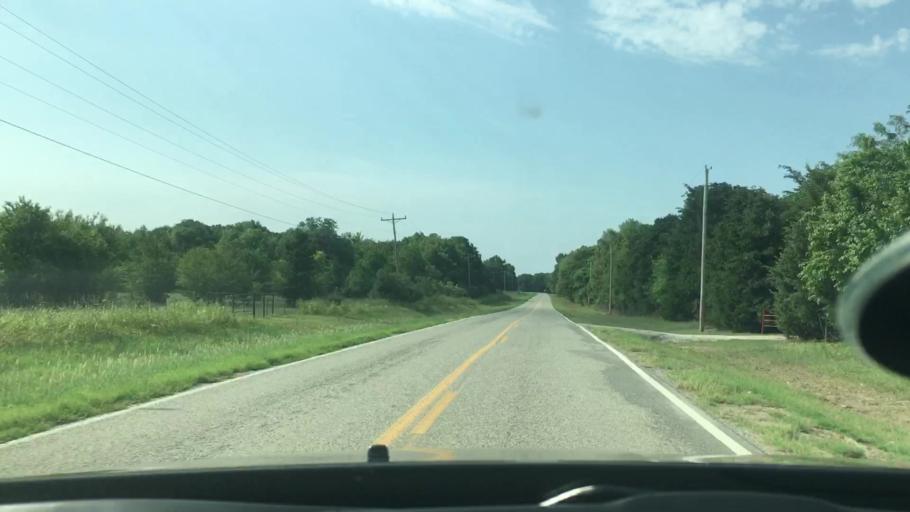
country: US
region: Oklahoma
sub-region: Johnston County
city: Tishomingo
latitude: 34.1746
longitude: -96.5838
